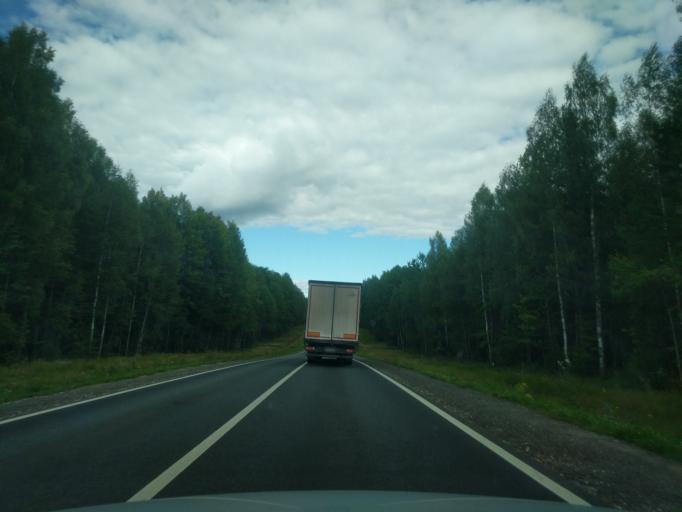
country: RU
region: Kostroma
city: Kadyy
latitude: 57.8467
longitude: 43.4656
